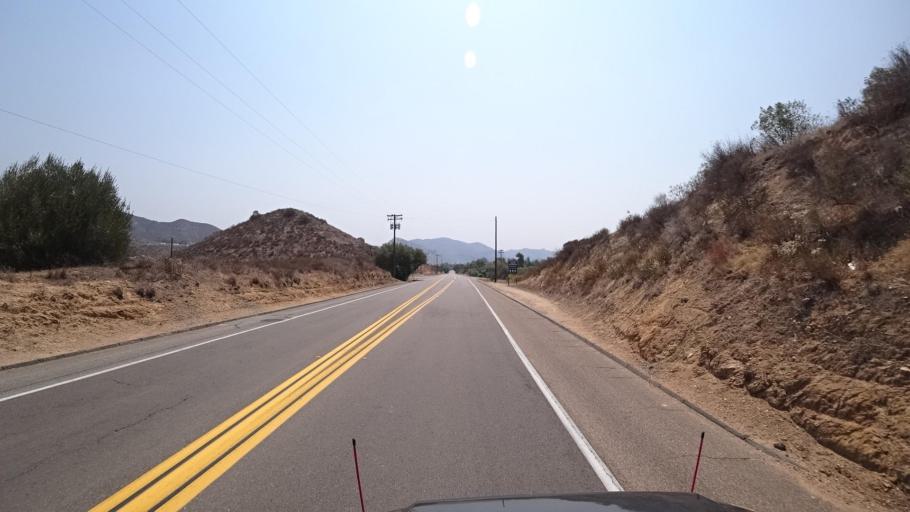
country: US
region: California
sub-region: San Diego County
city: Rainbow
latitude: 33.3658
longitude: -117.1646
